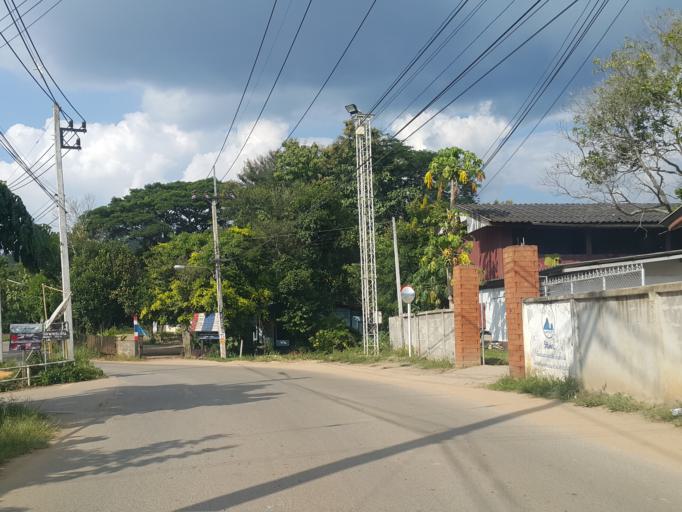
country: TH
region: Chiang Mai
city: Mae Chaem
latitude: 18.5120
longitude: 98.3589
